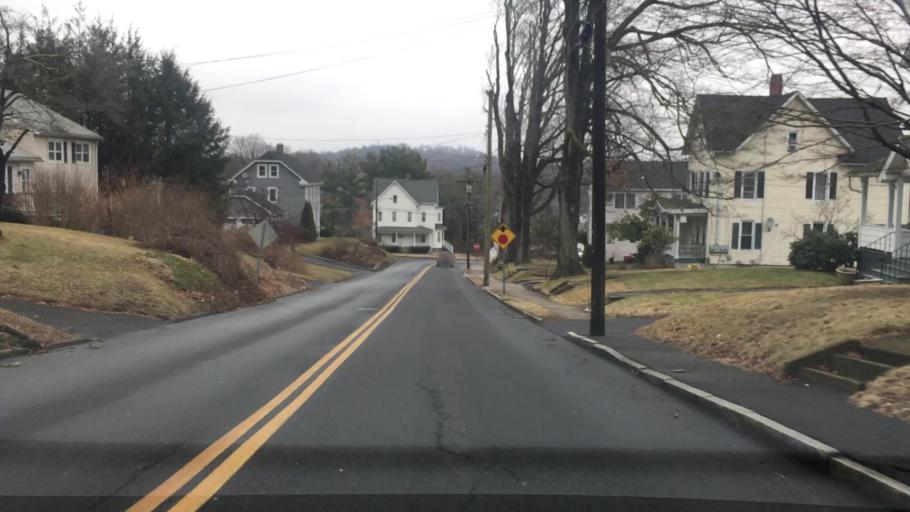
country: US
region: Connecticut
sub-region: Fairfield County
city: Danbury
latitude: 41.3848
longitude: -73.4485
